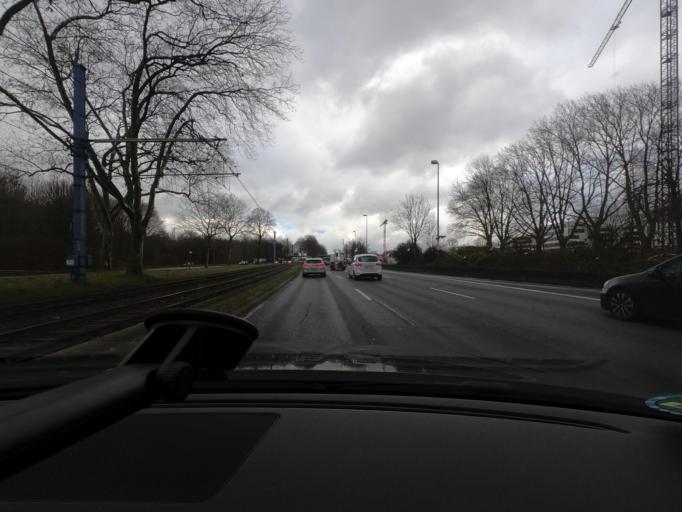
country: DE
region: North Rhine-Westphalia
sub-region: Regierungsbezirk Arnsberg
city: Dortmund
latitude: 51.5050
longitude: 7.5228
